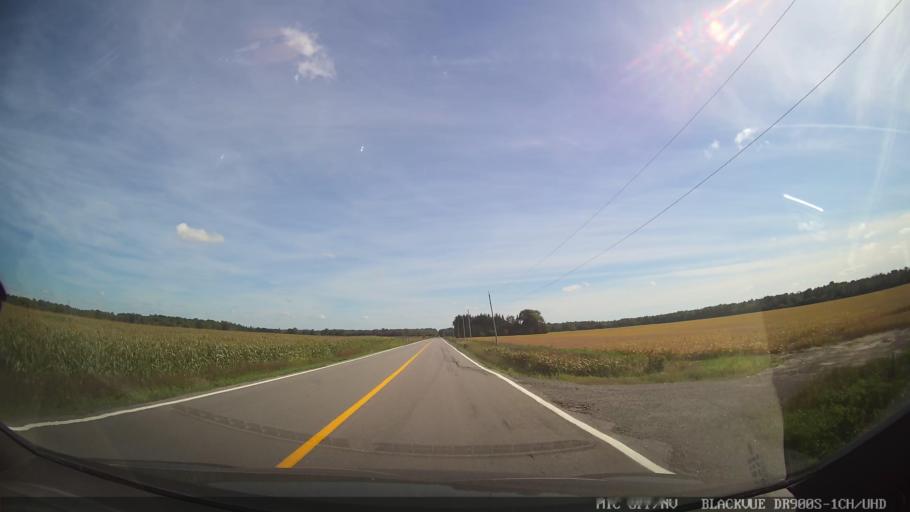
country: CA
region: Ontario
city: Bells Corners
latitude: 45.0983
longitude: -75.7092
